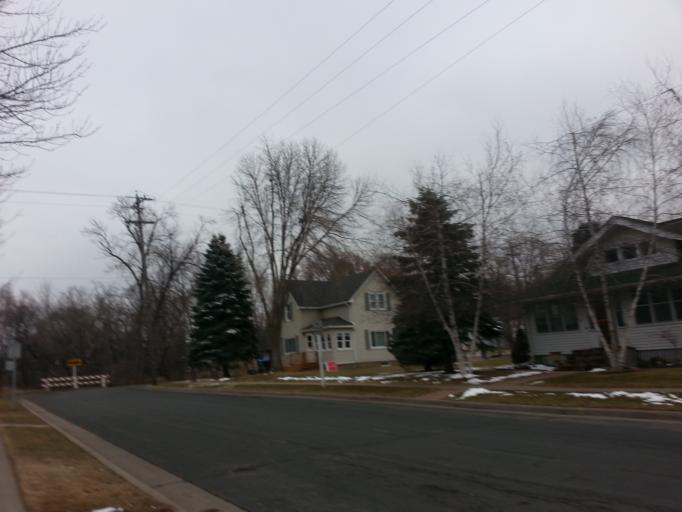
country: US
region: Wisconsin
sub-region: Saint Croix County
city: Hudson
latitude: 44.9833
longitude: -92.7588
